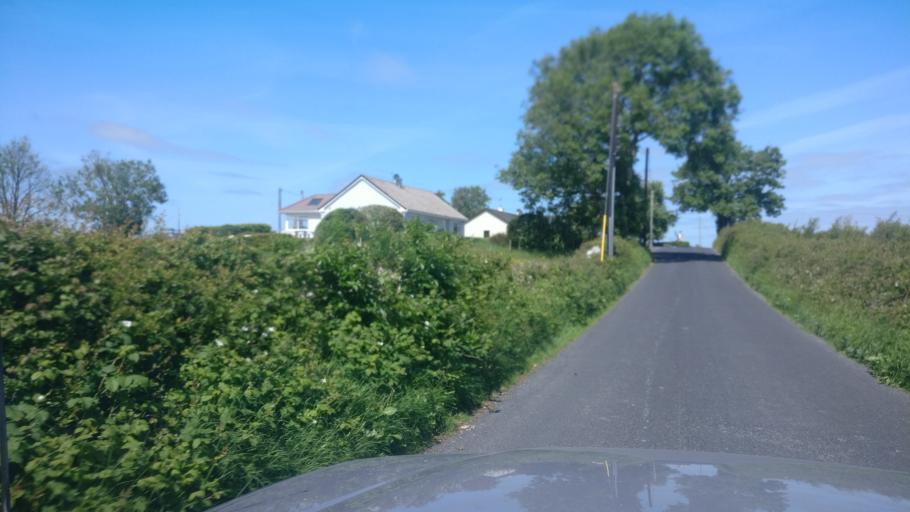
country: IE
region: Connaught
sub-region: County Galway
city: Gort
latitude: 53.0861
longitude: -8.8016
